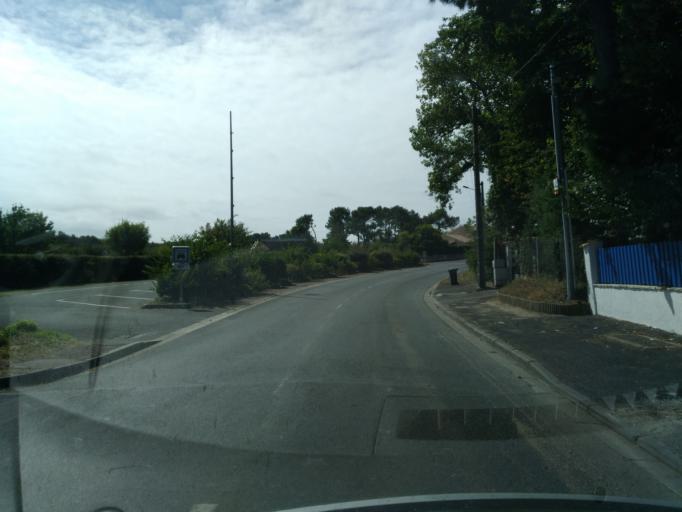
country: FR
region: Poitou-Charentes
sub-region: Departement de la Charente-Maritime
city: Vaux-sur-Mer
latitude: 45.6629
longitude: -1.0719
